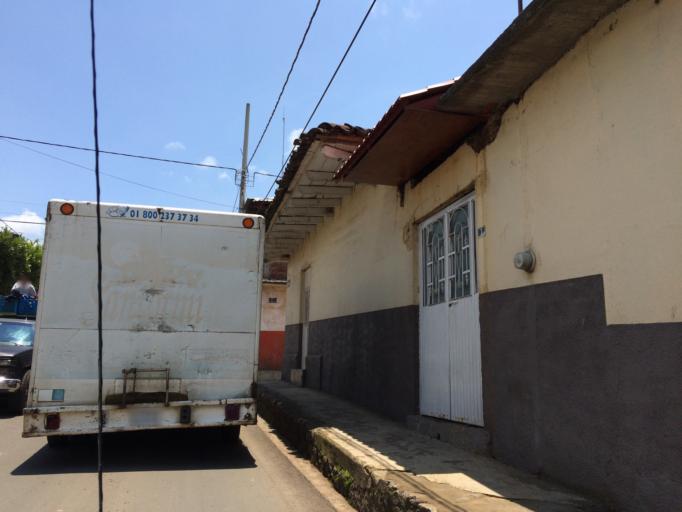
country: MX
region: Michoacan
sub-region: Periban
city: San Francisco Periban
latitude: 19.5561
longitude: -102.3988
